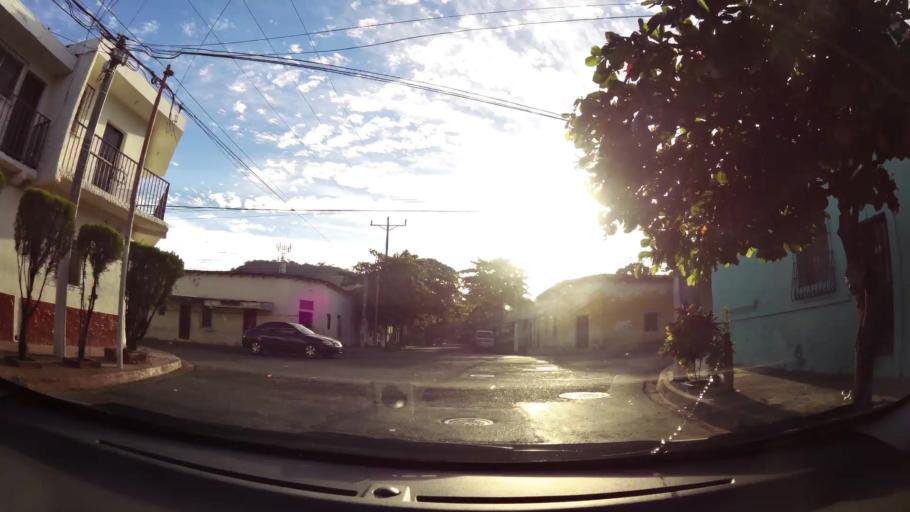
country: SV
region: Santa Ana
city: Santa Ana
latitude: 13.9923
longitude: -89.5471
